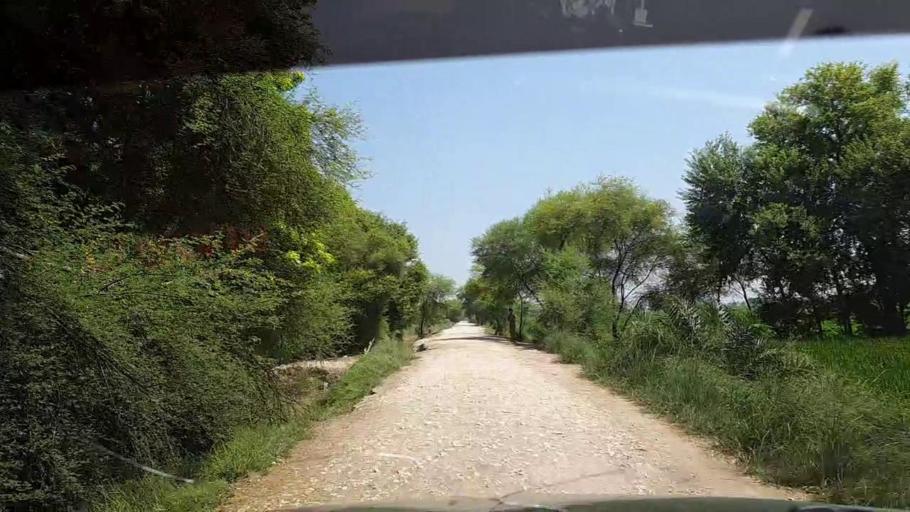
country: PK
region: Sindh
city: Ghauspur
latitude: 28.1713
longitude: 69.0617
